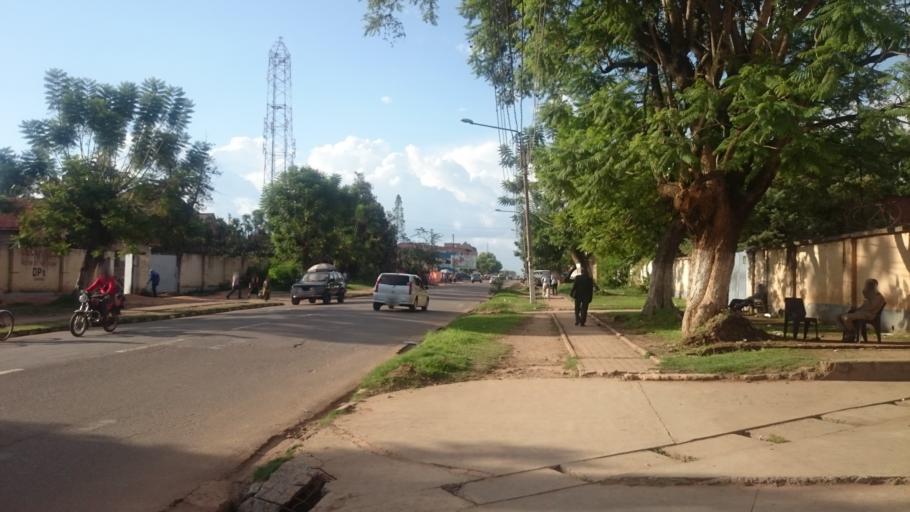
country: CD
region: Katanga
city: Lubumbashi
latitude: -11.6720
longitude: 27.4824
